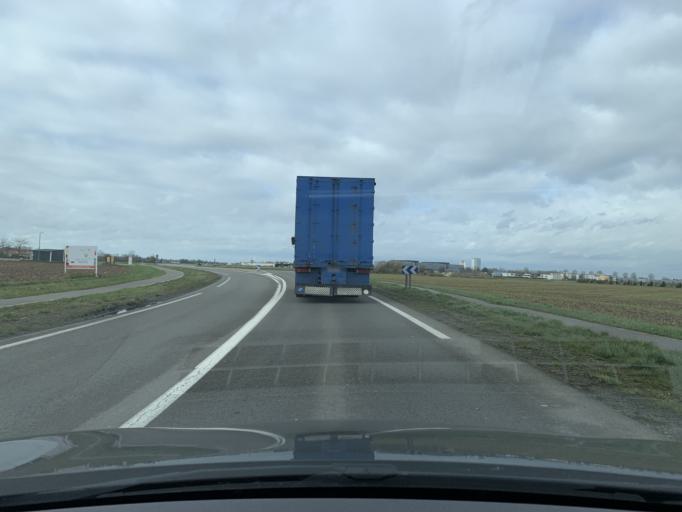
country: FR
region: Nord-Pas-de-Calais
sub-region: Departement du Nord
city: Goeulzin
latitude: 50.3290
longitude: 3.1092
